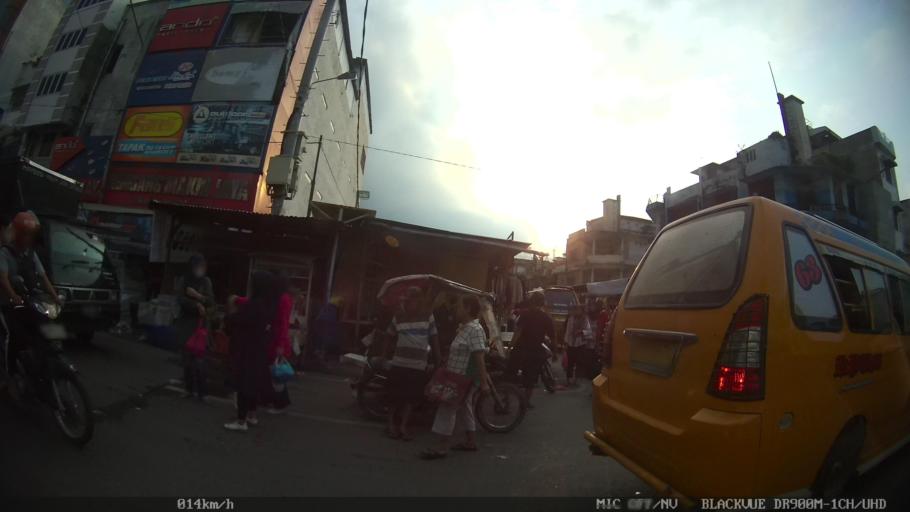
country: ID
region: North Sumatra
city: Medan
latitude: 3.5891
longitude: 98.6849
